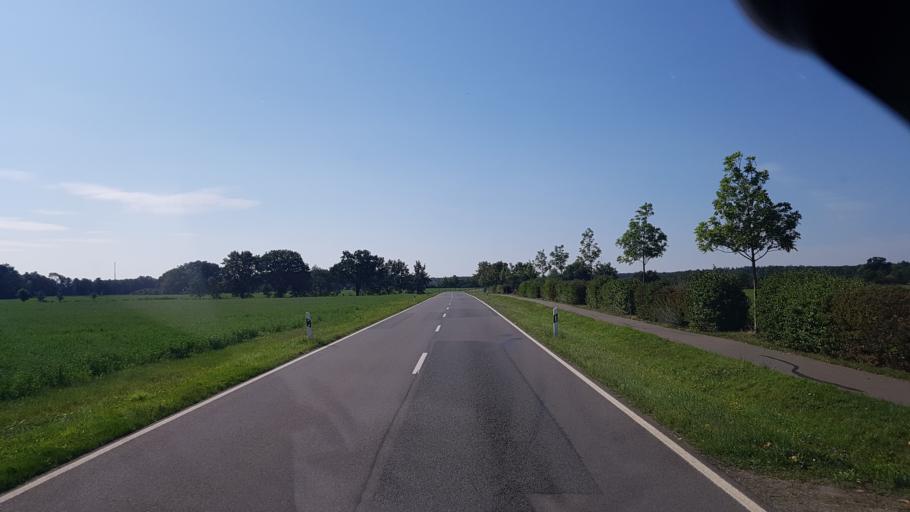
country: DE
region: Brandenburg
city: Vetschau
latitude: 51.7252
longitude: 14.0445
